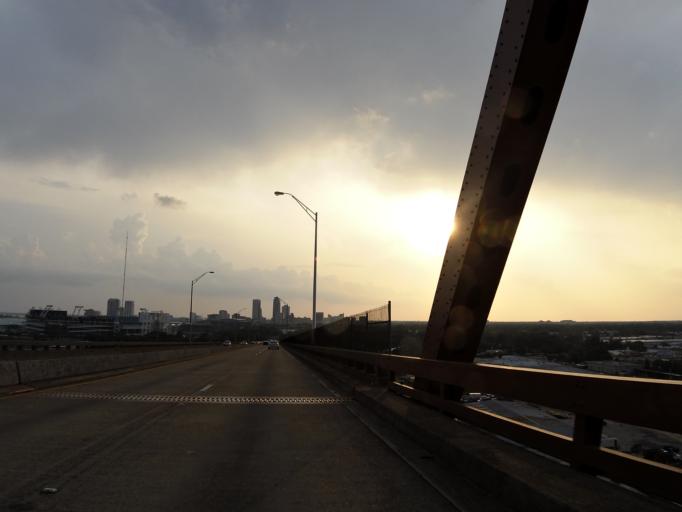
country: US
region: Florida
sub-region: Duval County
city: Jacksonville
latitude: 30.3274
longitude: -81.6267
